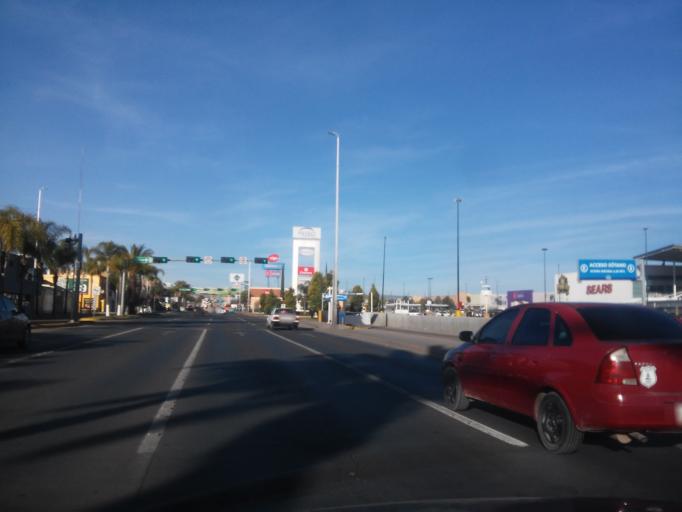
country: MX
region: Durango
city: Victoria de Durango
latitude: 24.0346
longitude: -104.6505
